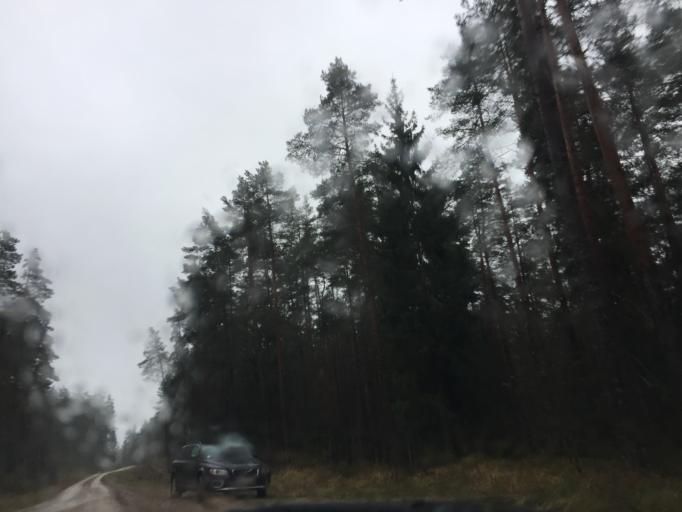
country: LV
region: Salas
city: Sala
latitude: 56.5107
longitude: 25.6968
